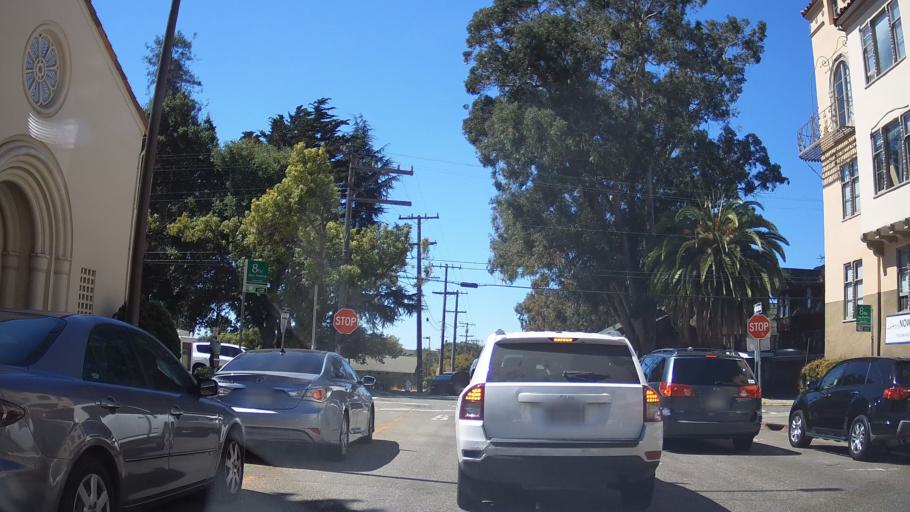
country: US
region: California
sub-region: Alameda County
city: Berkeley
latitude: 37.8663
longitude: -122.2560
